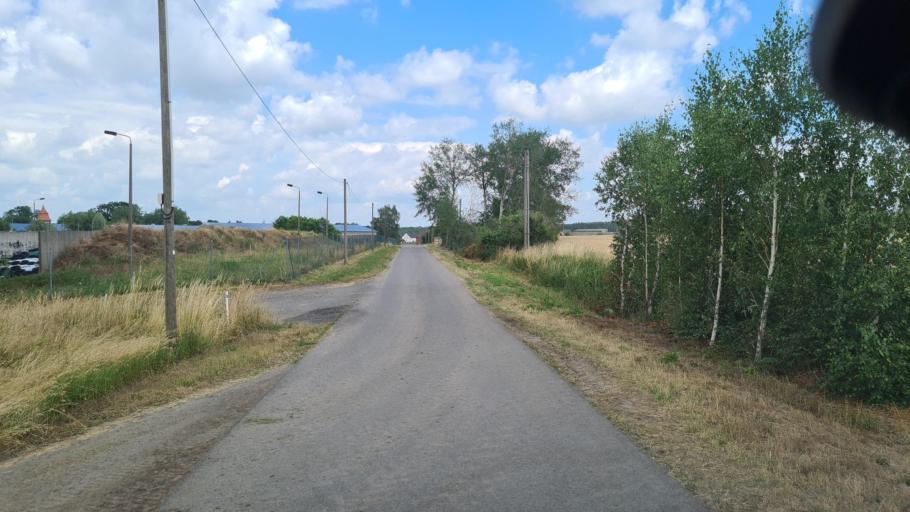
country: DE
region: Brandenburg
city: Calau
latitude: 51.7569
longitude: 13.9107
